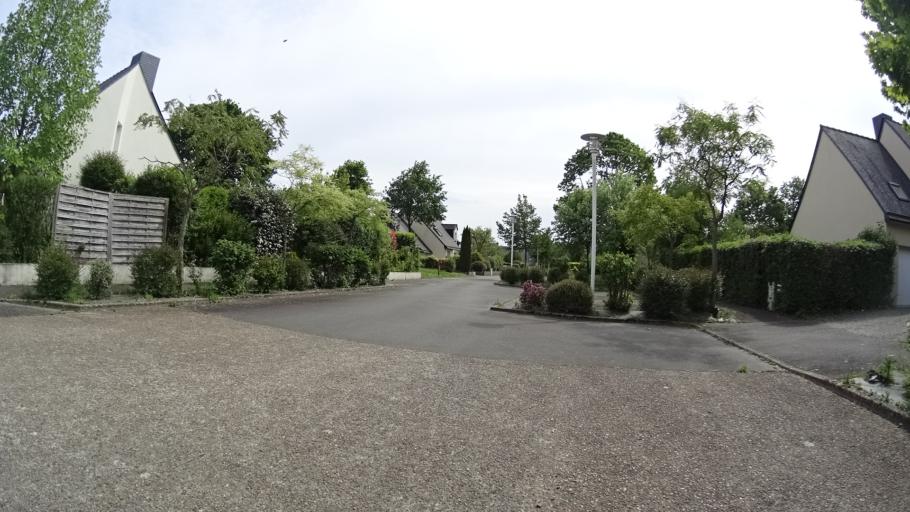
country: FR
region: Brittany
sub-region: Departement d'Ille-et-Vilaine
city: La Meziere
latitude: 48.2210
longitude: -1.7618
